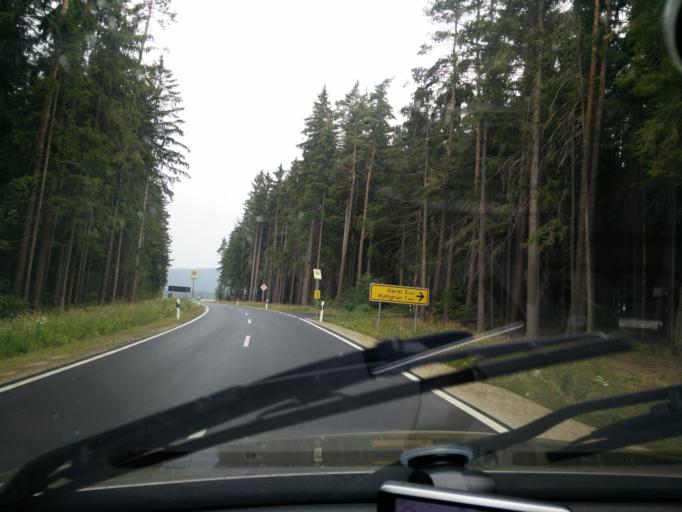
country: DE
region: Bavaria
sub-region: Upper Franconia
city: Trostau
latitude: 50.0473
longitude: 11.9418
